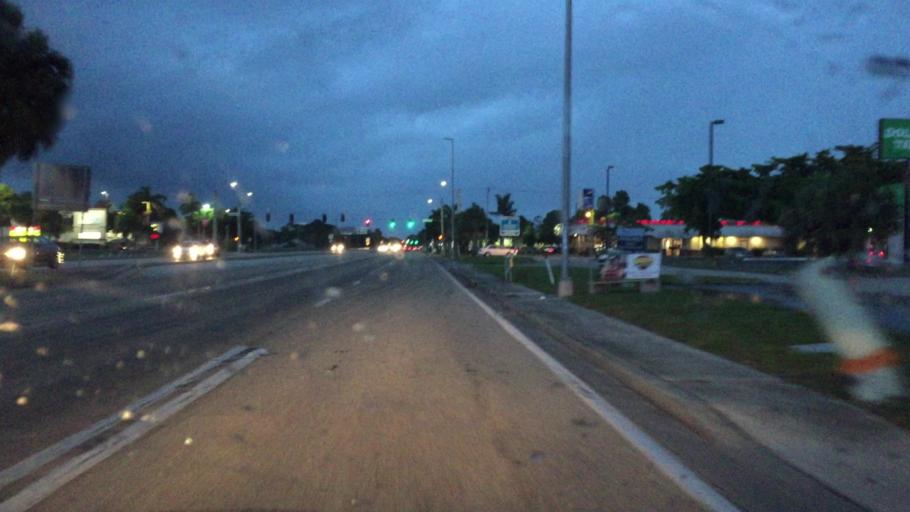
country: US
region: Florida
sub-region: Lee County
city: McGregor
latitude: 26.5565
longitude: -81.9056
